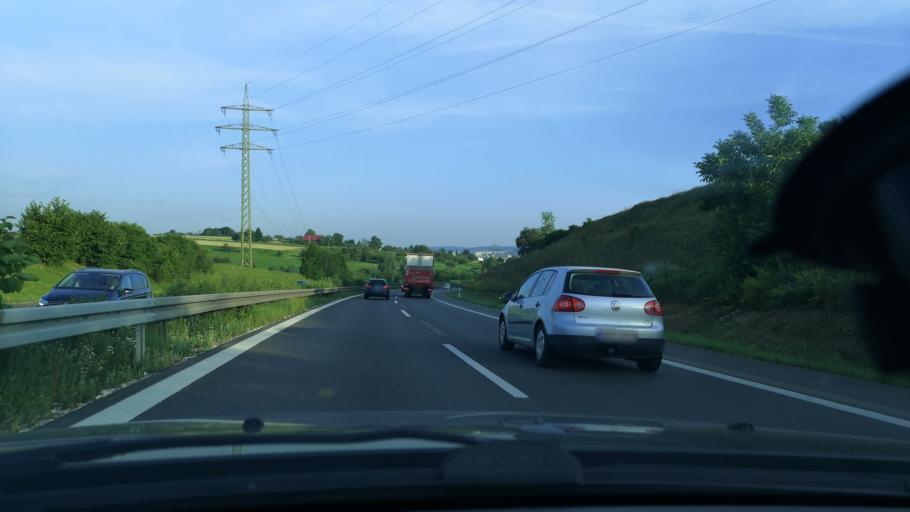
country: DE
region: Baden-Wuerttemberg
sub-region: Regierungsbezirk Stuttgart
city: Eislingen
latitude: 48.6818
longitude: 9.7075
